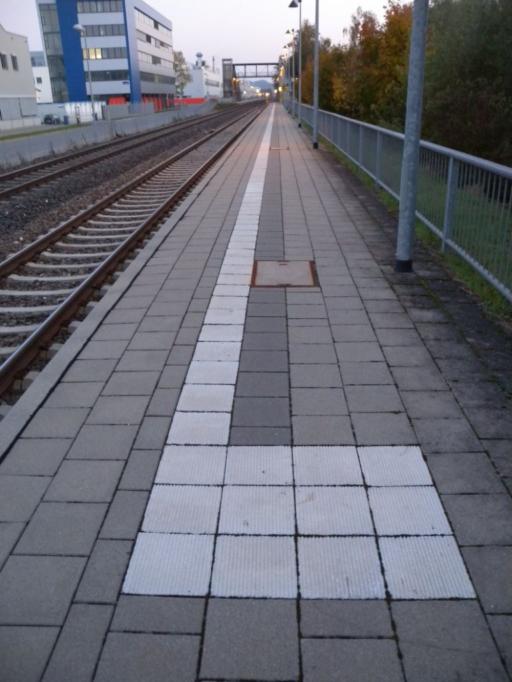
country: DE
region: Baden-Wuerttemberg
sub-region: Tuebingen Region
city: Biberach an der Riss
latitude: 48.0883
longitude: 9.8025
